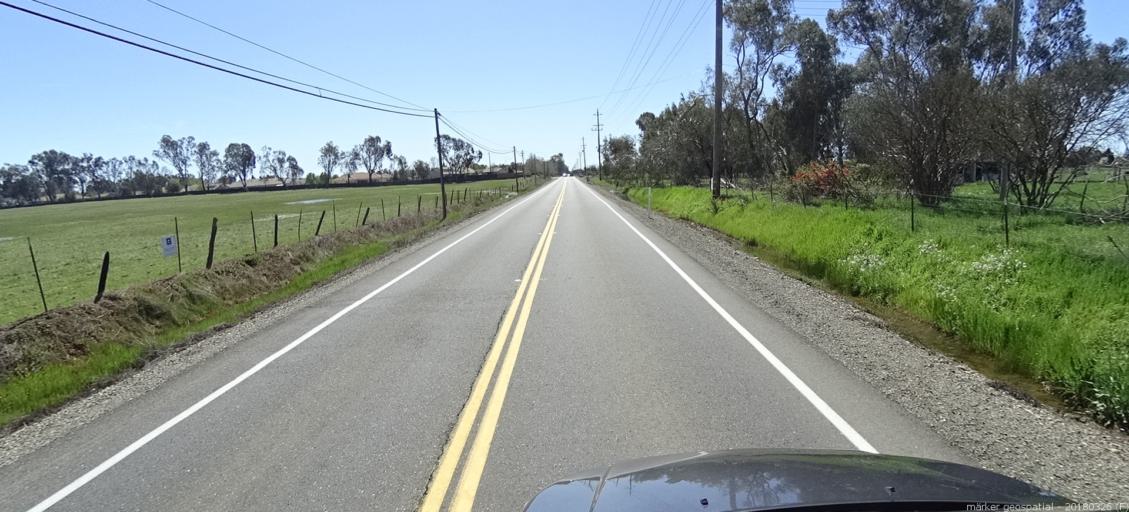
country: US
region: California
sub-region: Sacramento County
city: Vineyard
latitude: 38.4694
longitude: -121.2976
